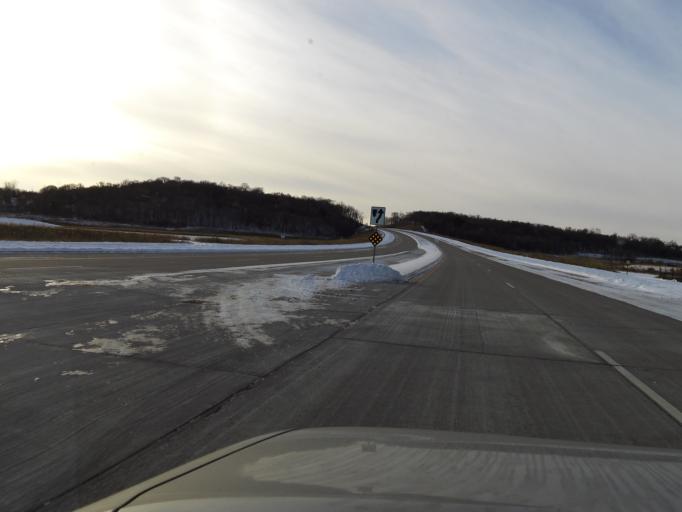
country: US
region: Minnesota
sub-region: Scott County
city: Prior Lake
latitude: 44.7623
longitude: -93.4388
